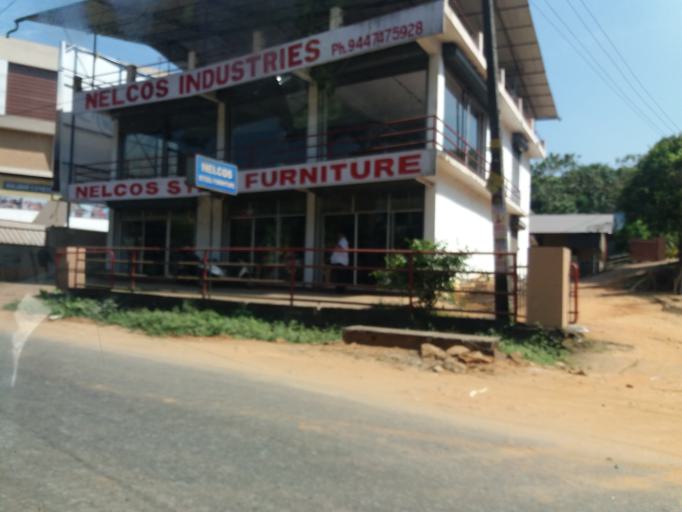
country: IN
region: Kerala
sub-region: Ernakulam
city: Muvattupuzha
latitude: 9.8907
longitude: 76.7069
